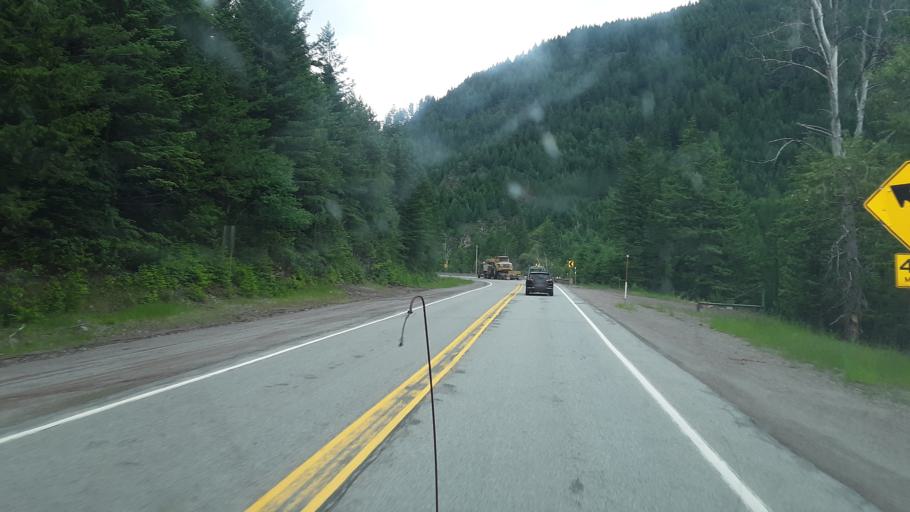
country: US
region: Montana
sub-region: Flathead County
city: Columbia Falls
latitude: 48.5001
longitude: -113.9294
